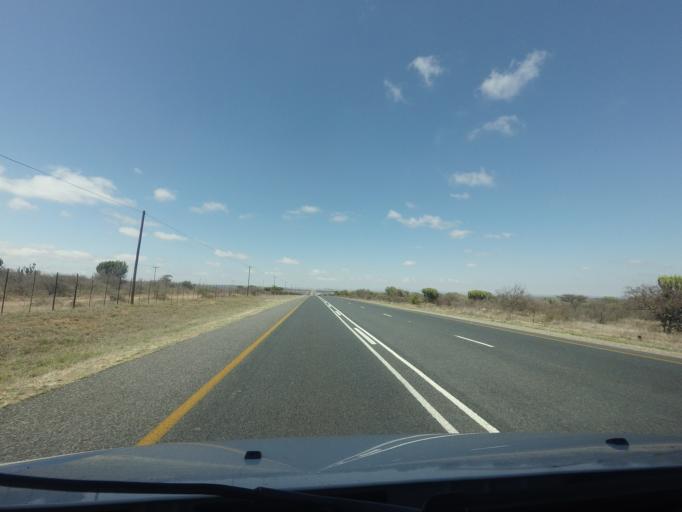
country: ZA
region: Limpopo
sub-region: Vhembe District Municipality
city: Louis Trichardt
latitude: -23.3756
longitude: 29.7689
